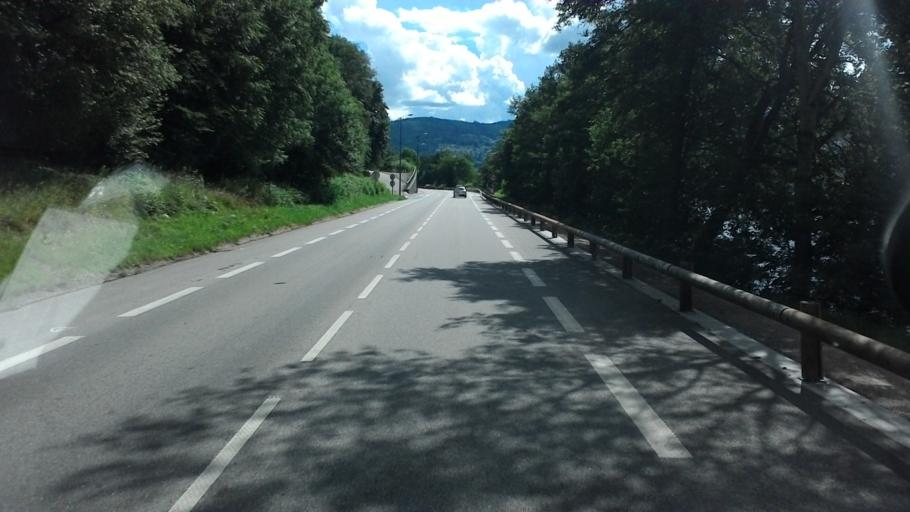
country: FR
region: Lorraine
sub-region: Departement des Vosges
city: Gerardmer
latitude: 48.0725
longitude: 6.8497
